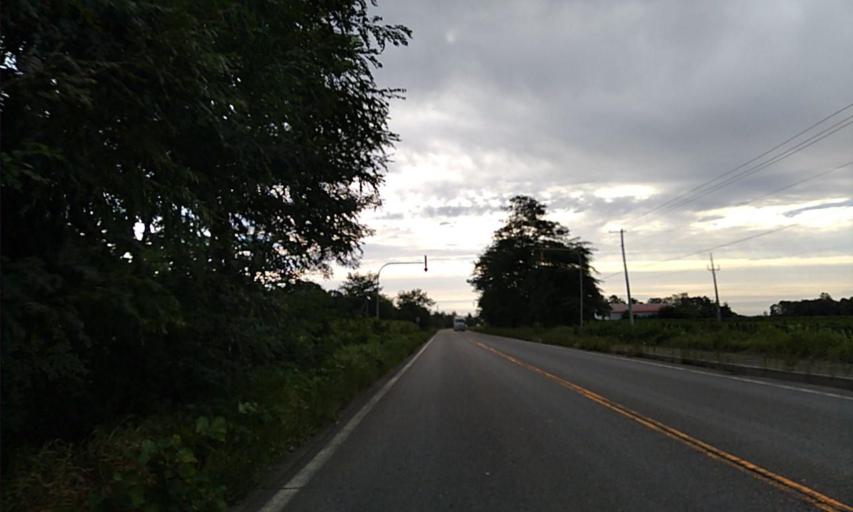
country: JP
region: Hokkaido
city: Obihiro
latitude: 42.9343
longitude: 142.9714
